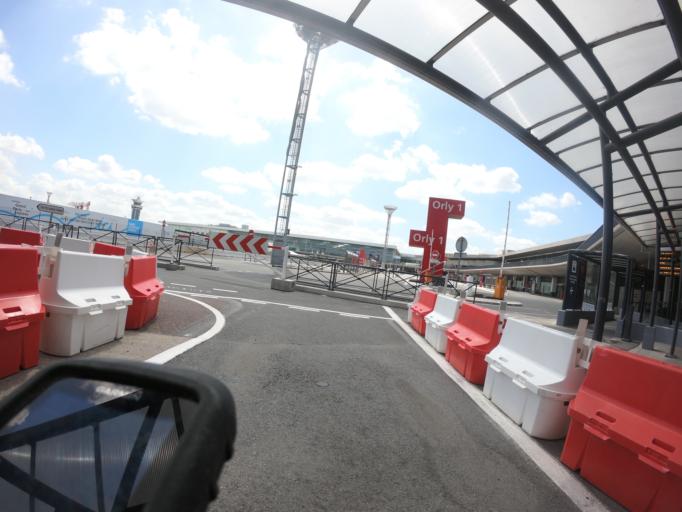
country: FR
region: Ile-de-France
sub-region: Departement de l'Essonne
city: Paray-Vieille-Poste
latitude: 48.7291
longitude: 2.3598
